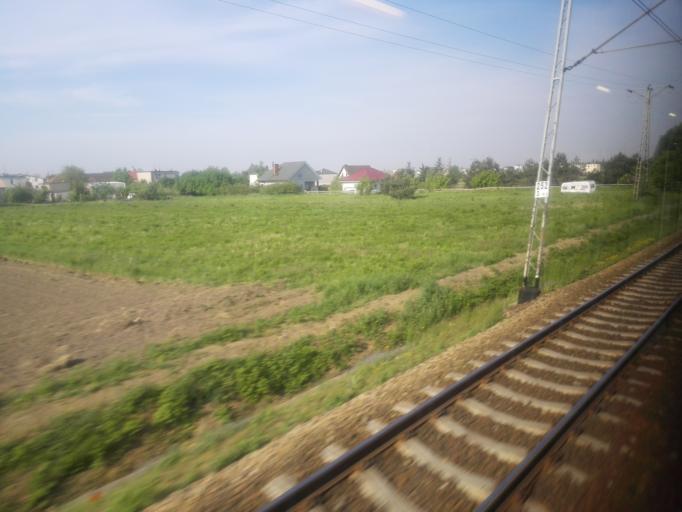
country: PL
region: Greater Poland Voivodeship
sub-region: Powiat wrzesinski
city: Wrzesnia
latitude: 52.3370
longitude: 17.5881
